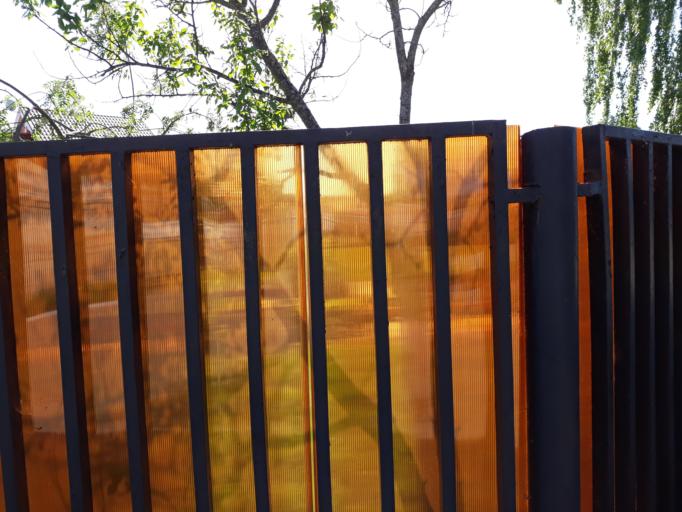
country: RU
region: Jaroslavl
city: Krasnyy Profintern
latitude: 57.8667
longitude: 40.2698
